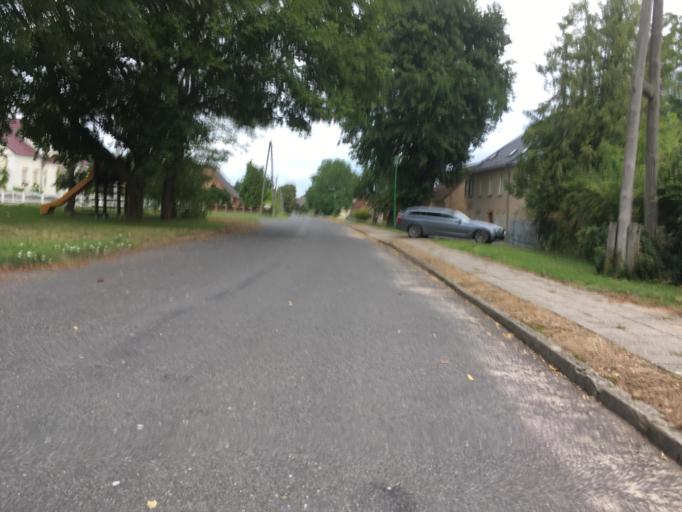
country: DE
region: Brandenburg
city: Prenzlau
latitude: 53.2611
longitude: 13.8484
